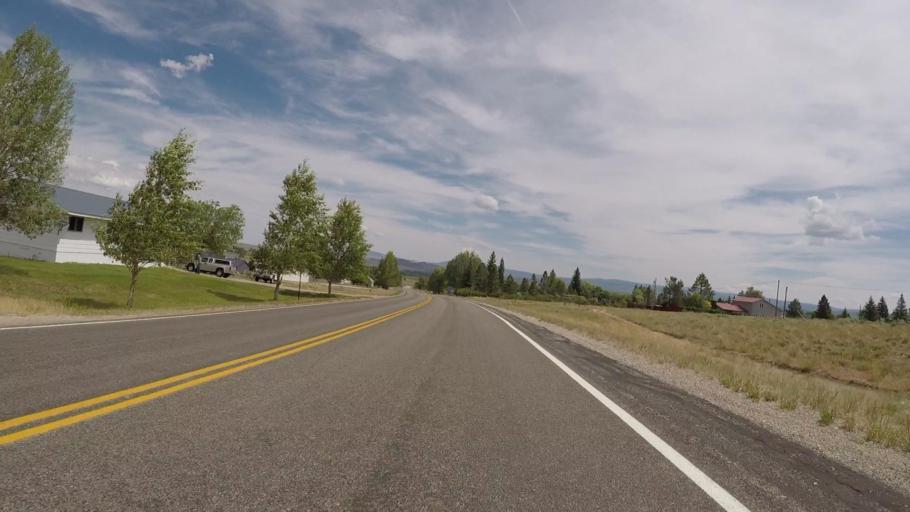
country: US
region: Wyoming
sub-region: Carbon County
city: Saratoga
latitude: 41.2052
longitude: -106.7990
